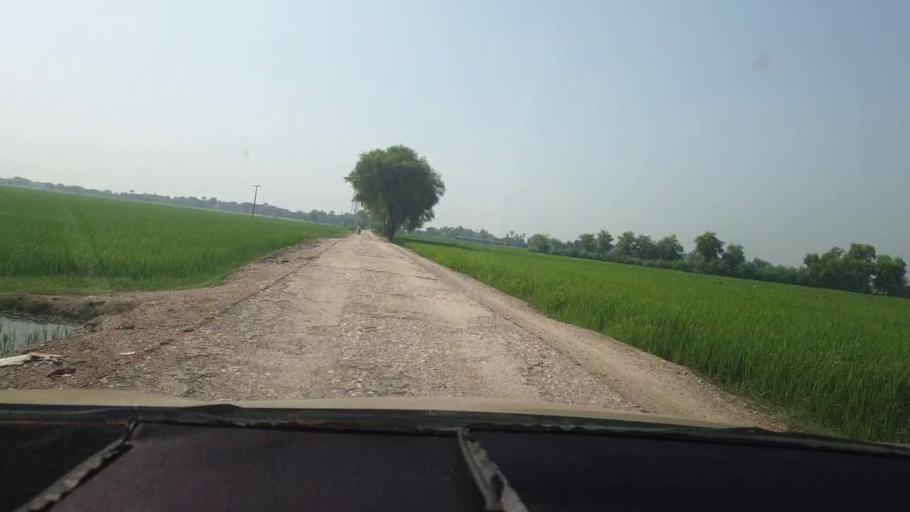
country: PK
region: Sindh
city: Kambar
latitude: 27.5643
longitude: 68.0577
